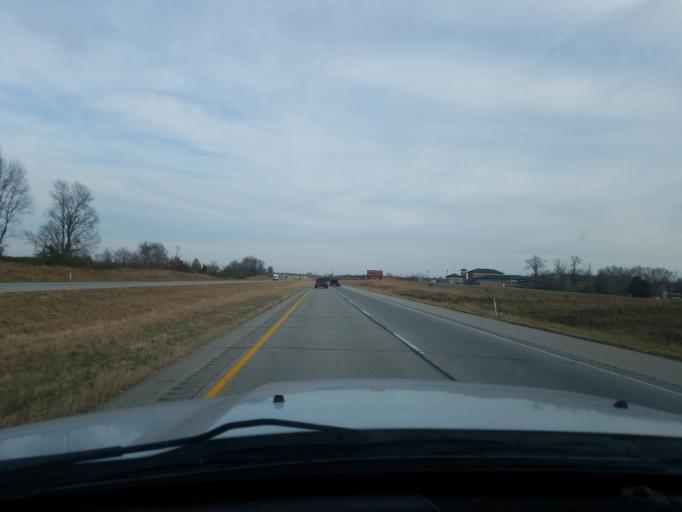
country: US
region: Indiana
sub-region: Harrison County
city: Corydon
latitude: 38.2400
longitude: -86.1529
